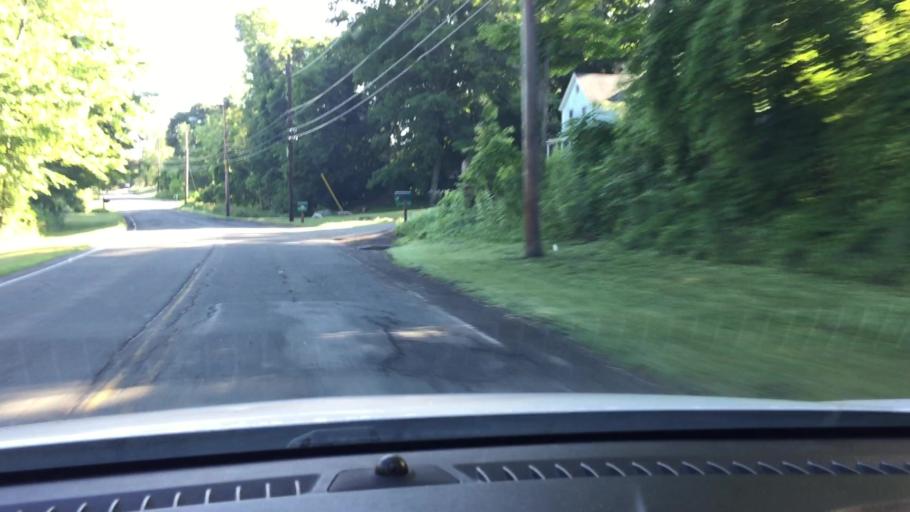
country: US
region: Massachusetts
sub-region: Berkshire County
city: Pittsfield
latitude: 42.4196
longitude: -73.2255
